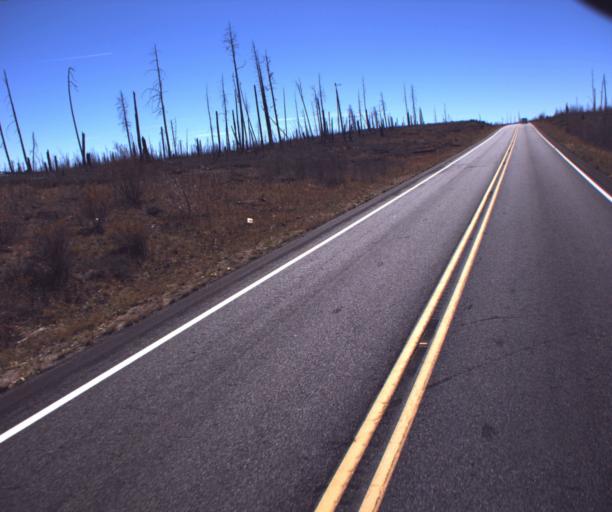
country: US
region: Arizona
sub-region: Coconino County
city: Fredonia
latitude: 36.5929
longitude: -112.1791
